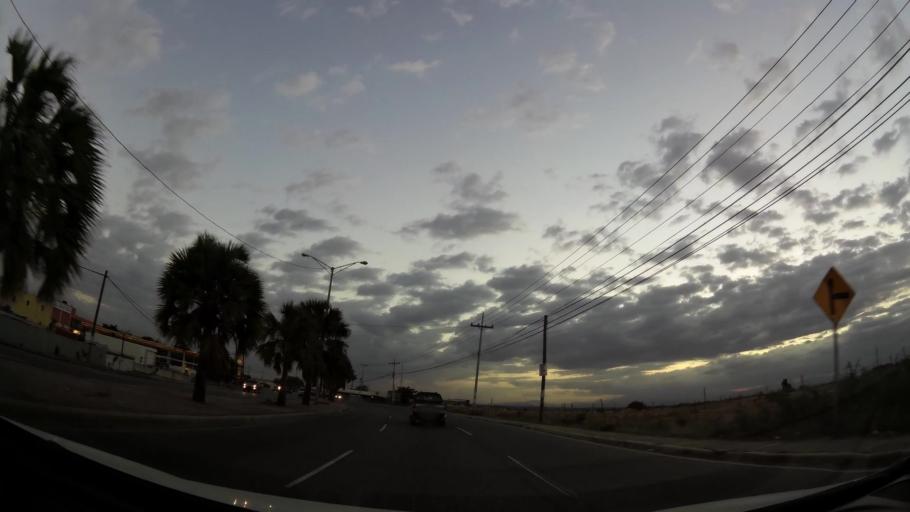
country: DO
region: Nacional
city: La Agustina
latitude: 18.5552
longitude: -69.9437
